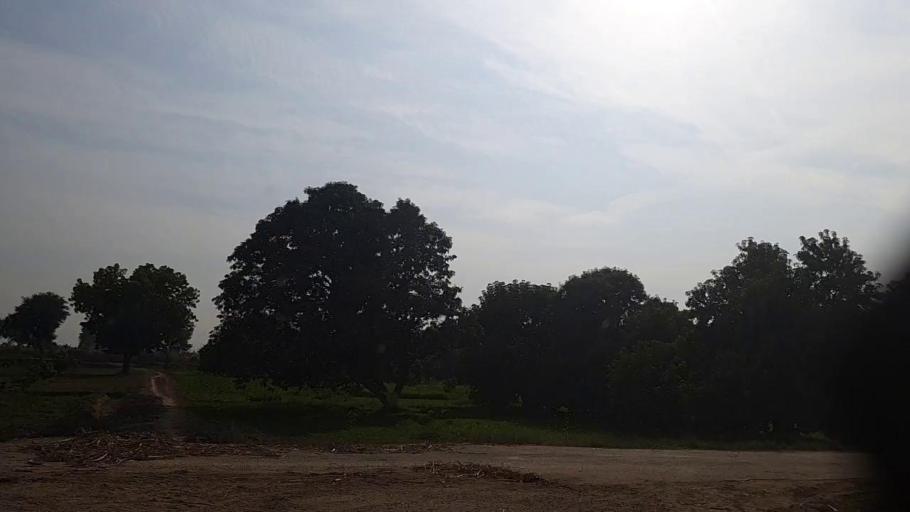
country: PK
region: Sindh
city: Daur
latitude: 26.3994
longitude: 68.2132
